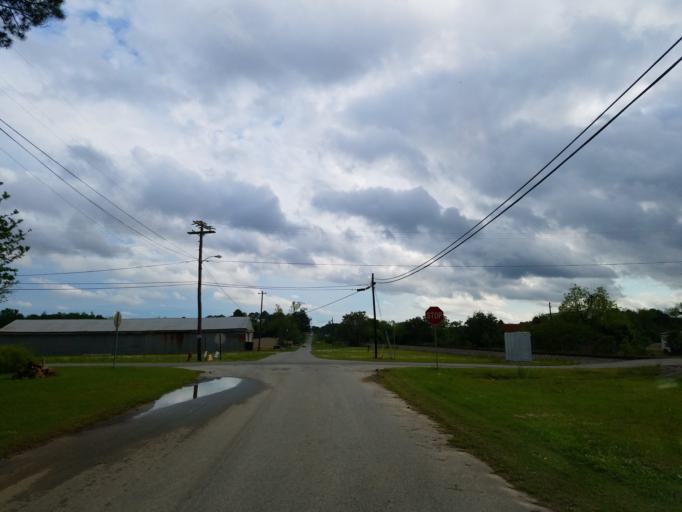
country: US
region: Georgia
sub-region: Dooly County
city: Unadilla
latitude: 32.2591
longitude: -83.7360
